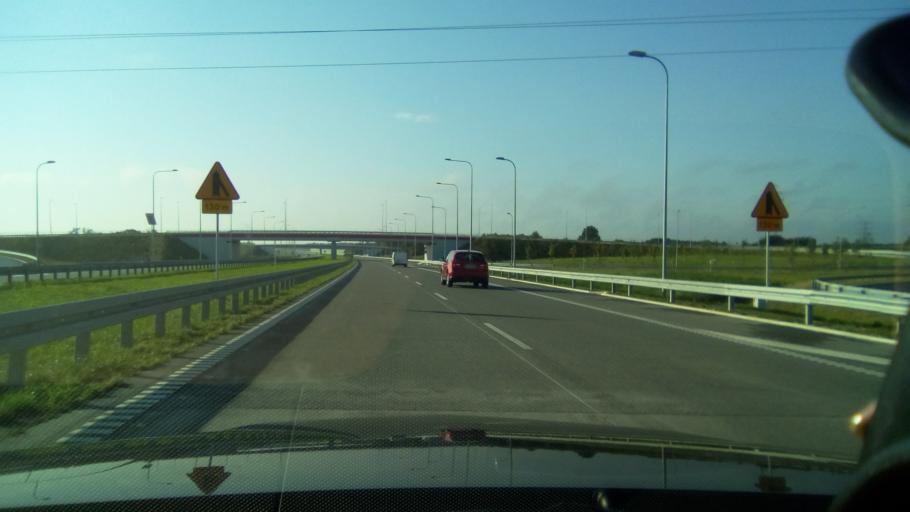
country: PL
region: Silesian Voivodeship
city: Wozniki
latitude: 50.5994
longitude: 19.0334
